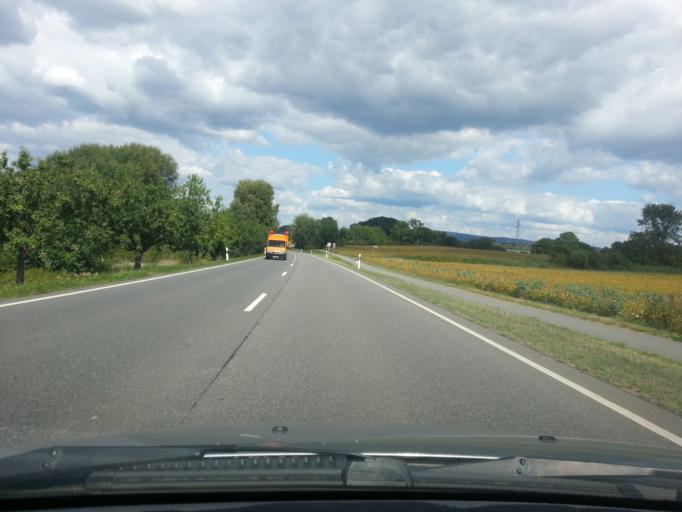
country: DE
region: Baden-Wuerttemberg
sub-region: Karlsruhe Region
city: Malsch
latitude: 49.2634
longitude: 8.6676
